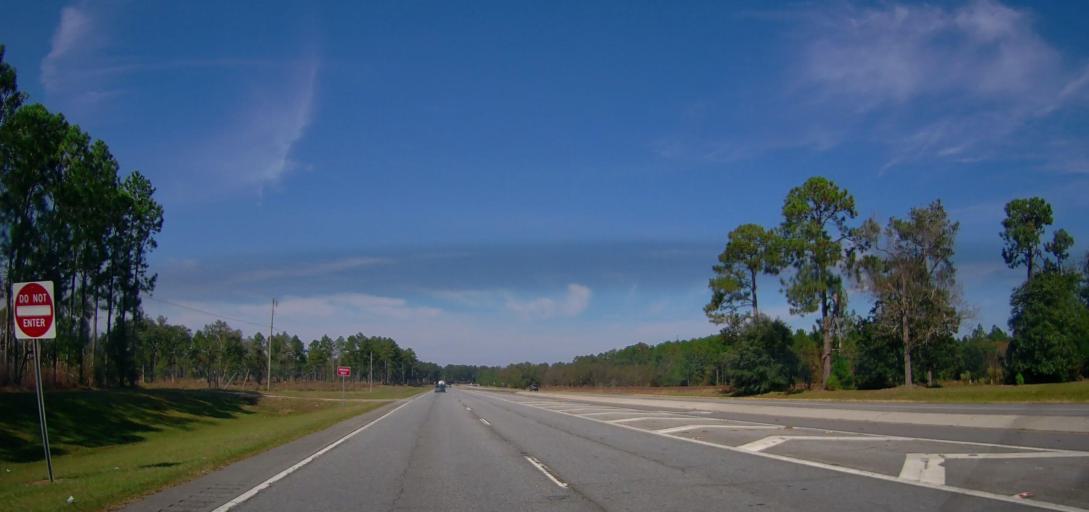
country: US
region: Georgia
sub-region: Lee County
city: Leesburg
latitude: 31.7431
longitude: -83.9872
